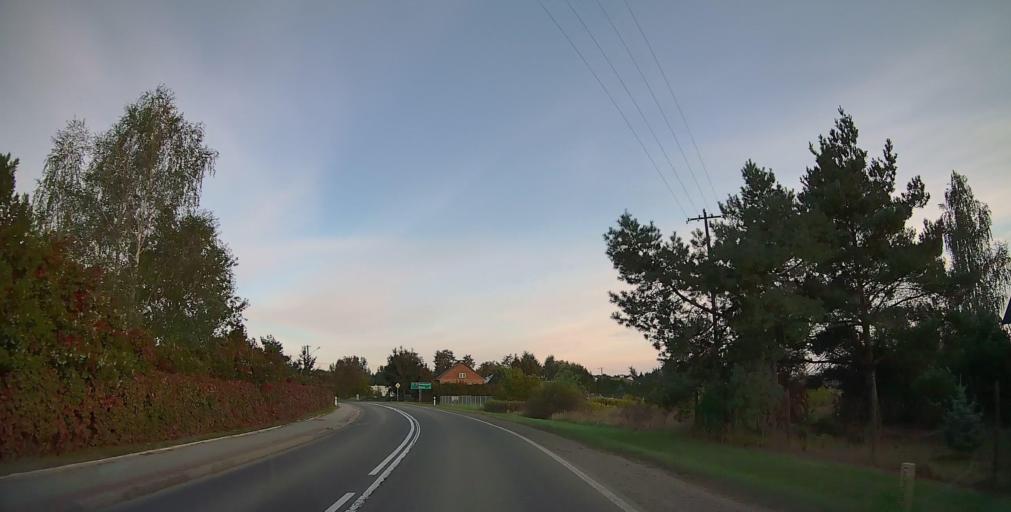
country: PL
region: Masovian Voivodeship
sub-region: Powiat garwolinski
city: Wilga
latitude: 51.8373
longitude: 21.2978
